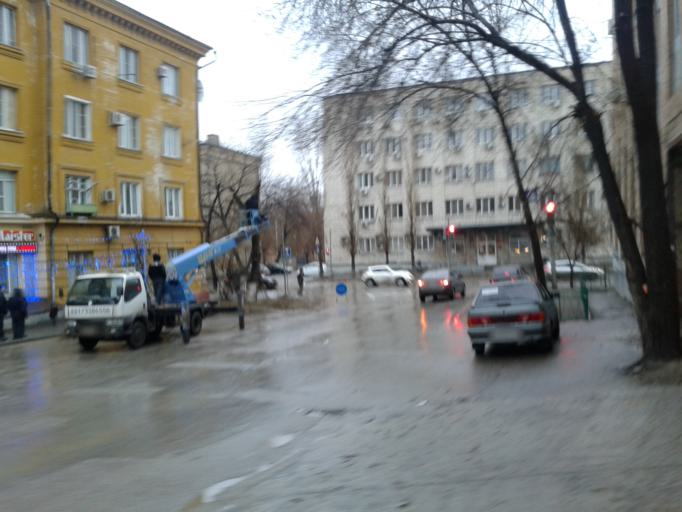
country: RU
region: Volgograd
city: Volgograd
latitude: 48.6942
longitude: 44.4882
